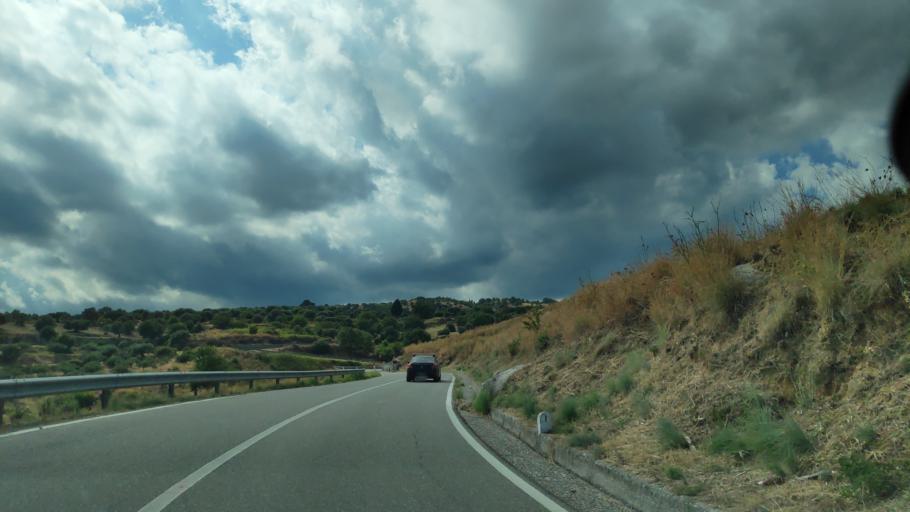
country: IT
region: Calabria
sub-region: Provincia di Catanzaro
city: Santa Caterina dello Ionio
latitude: 38.5240
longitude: 16.5360
